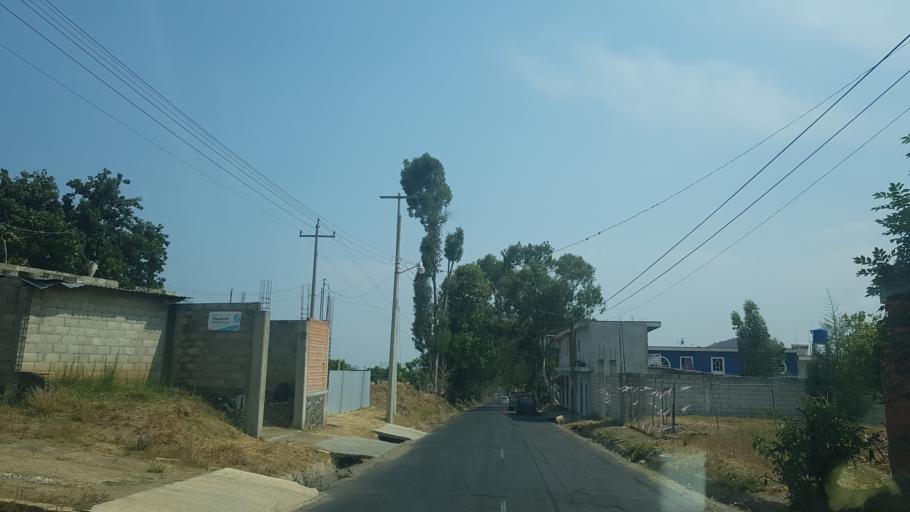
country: MX
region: Puebla
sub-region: Tianguismanalco
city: San Martin Tlapala
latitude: 18.9605
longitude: -98.4593
